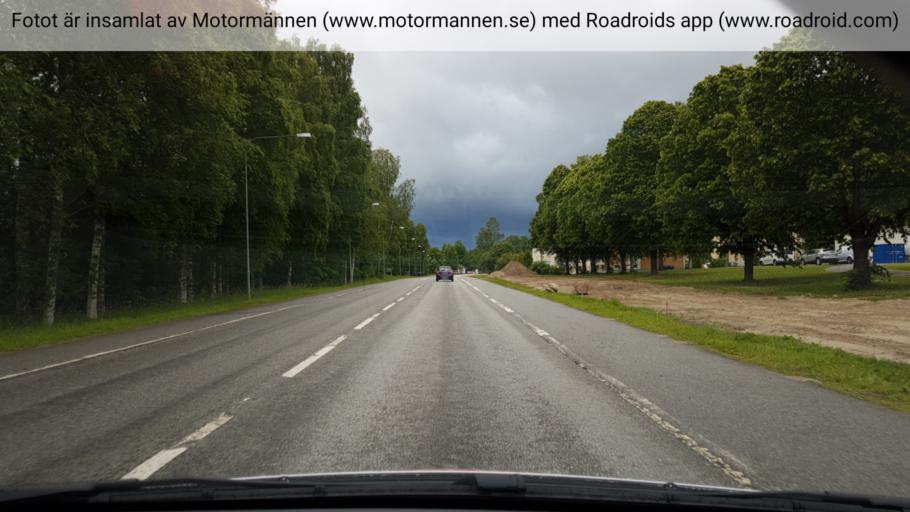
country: SE
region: OErebro
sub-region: Ljusnarsbergs Kommun
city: Kopparberg
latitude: 59.8708
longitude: 15.0116
